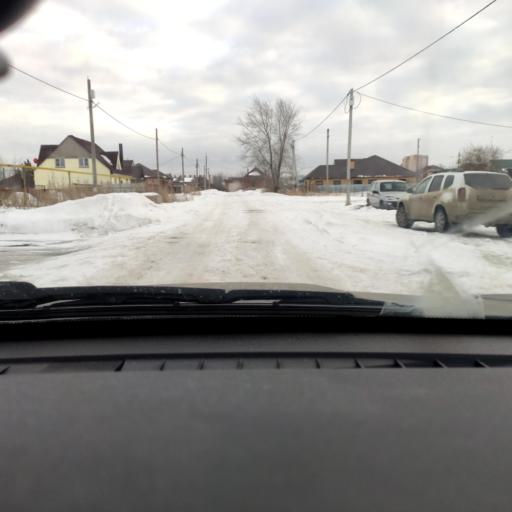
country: RU
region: Samara
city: Tol'yatti
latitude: 53.5523
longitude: 49.4037
